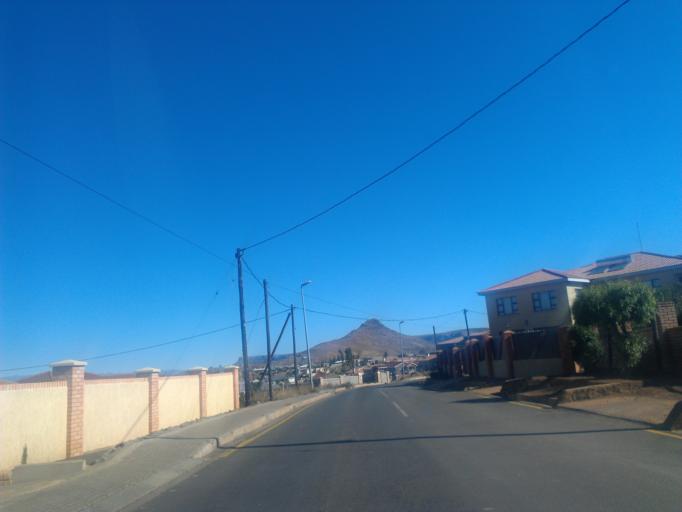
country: LS
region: Maseru
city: Maseru
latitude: -29.3436
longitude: 27.4479
